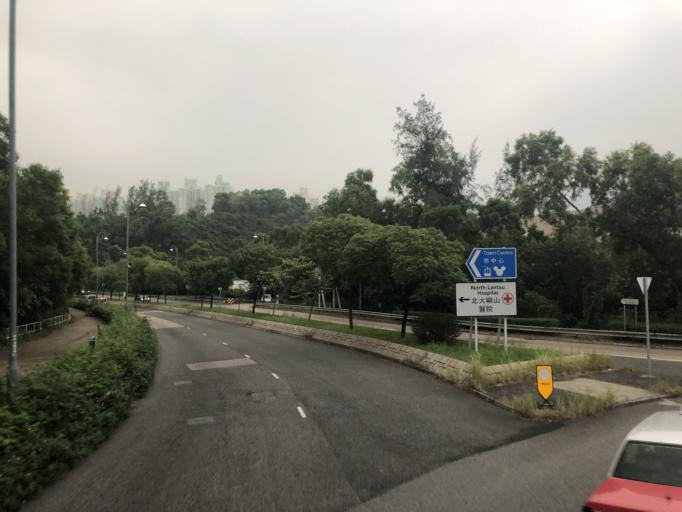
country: HK
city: Tai O
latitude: 22.2902
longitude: 113.9373
